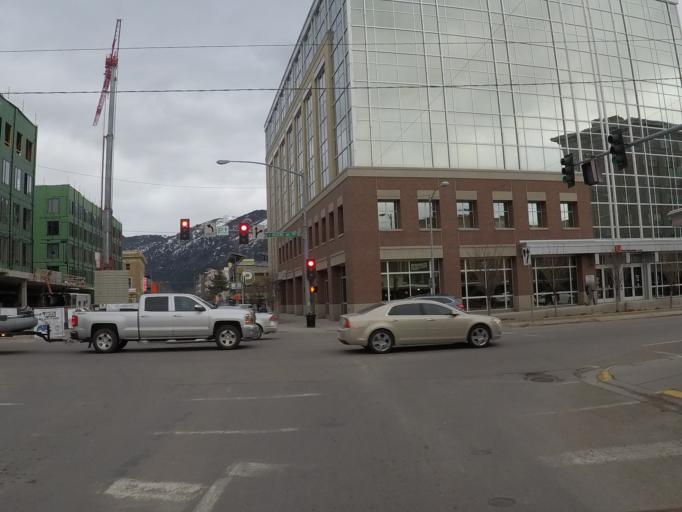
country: US
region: Montana
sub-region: Missoula County
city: Missoula
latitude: 46.8702
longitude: -113.9956
